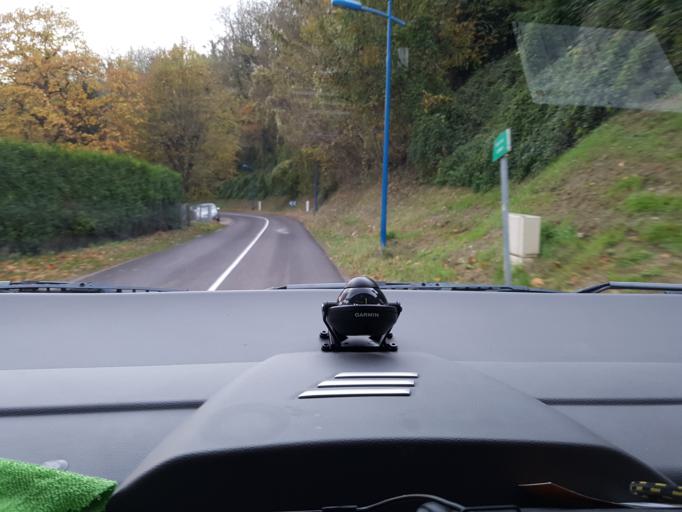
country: FR
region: Haute-Normandie
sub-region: Departement de la Seine-Maritime
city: Martin-Eglise
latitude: 49.9390
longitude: 1.1285
